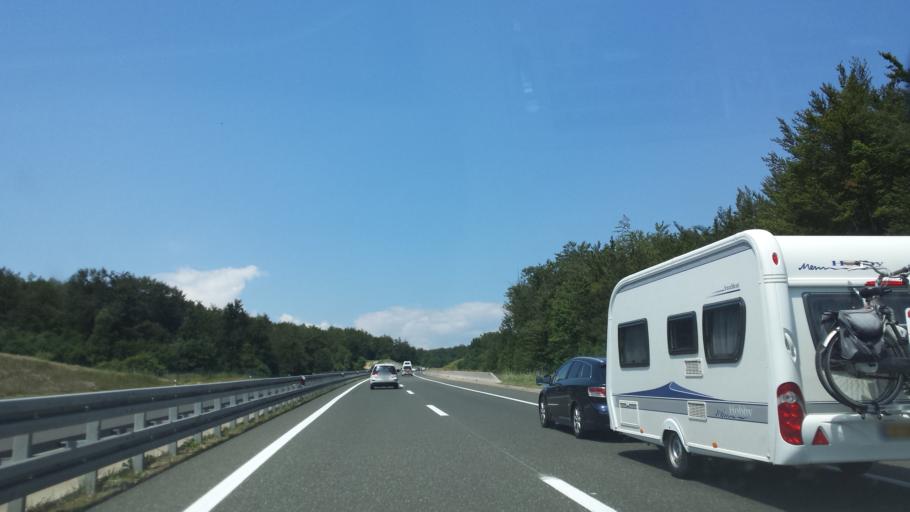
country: HR
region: Primorsko-Goranska
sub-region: Grad Delnice
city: Delnice
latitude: 45.3832
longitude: 14.8438
